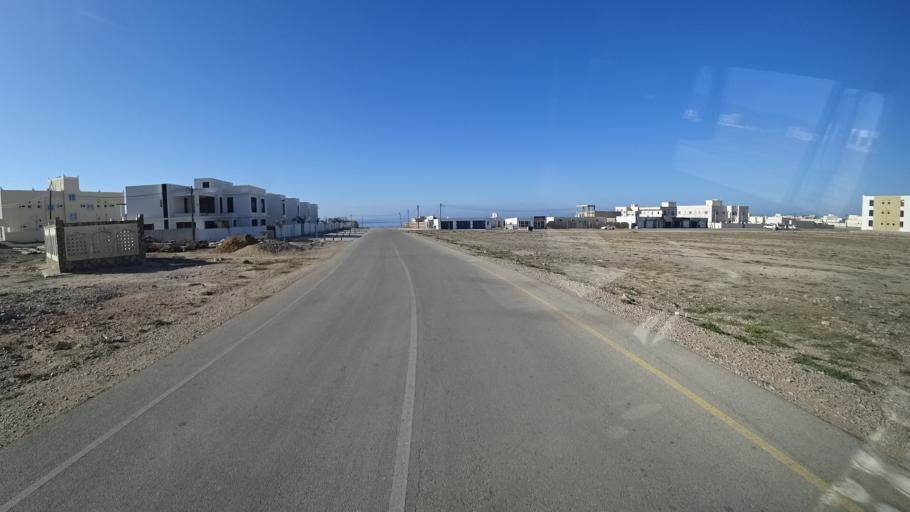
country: OM
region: Zufar
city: Salalah
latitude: 16.9801
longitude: 54.6961
